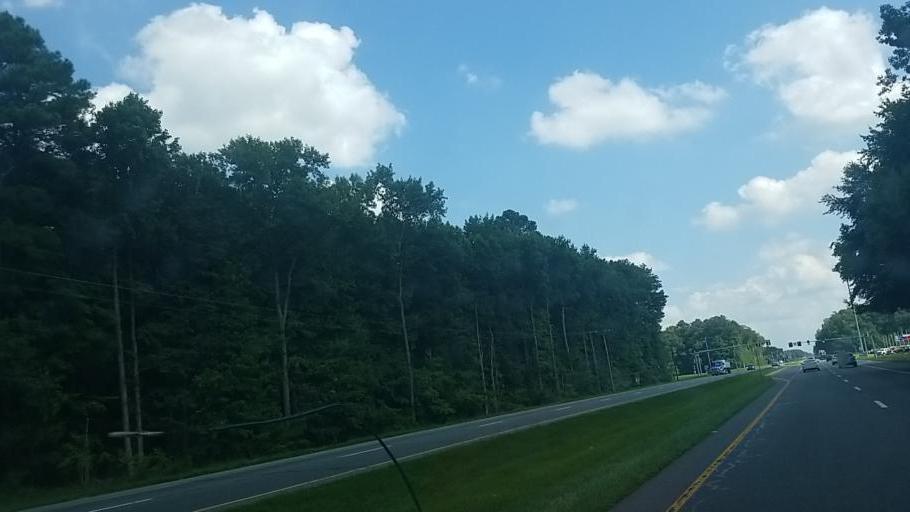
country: US
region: Delaware
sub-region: Sussex County
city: Georgetown
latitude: 38.6728
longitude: -75.3873
